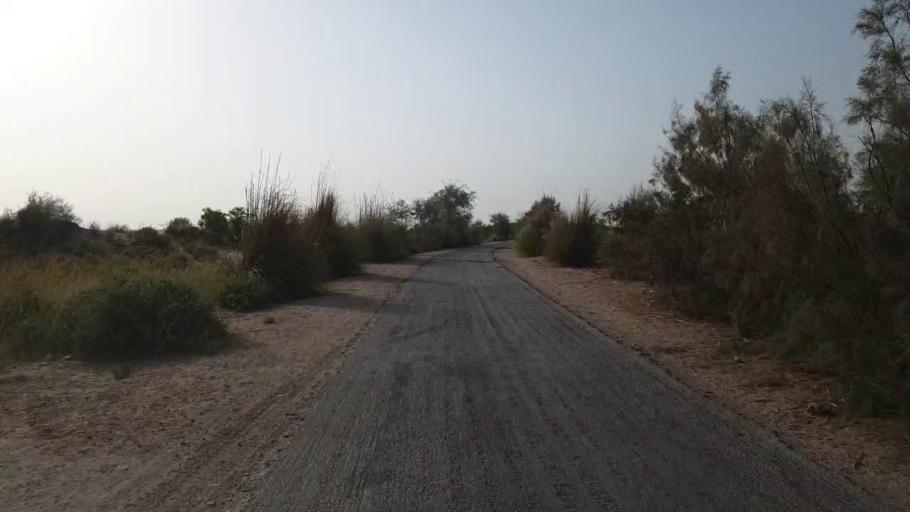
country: PK
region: Sindh
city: Jam Sahib
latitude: 26.4909
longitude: 68.8584
